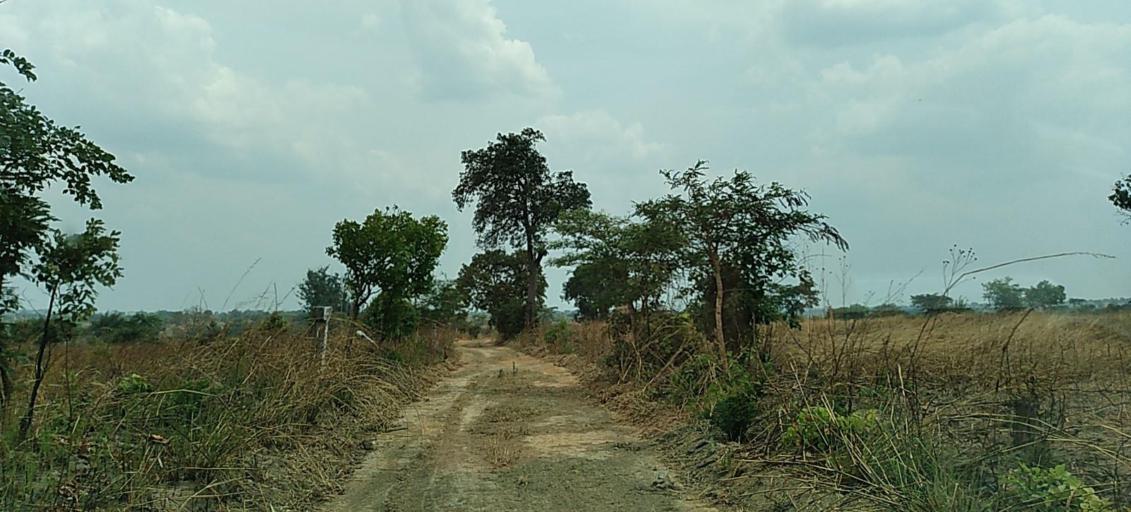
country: ZM
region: Copperbelt
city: Chililabombwe
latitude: -12.3581
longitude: 27.8000
